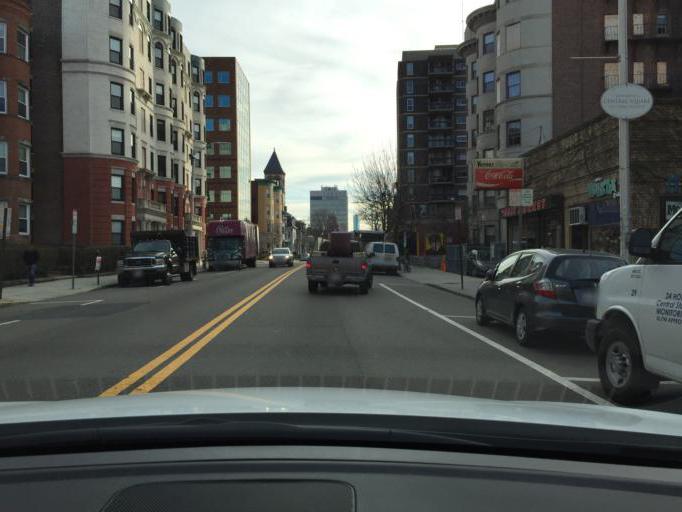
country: US
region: Massachusetts
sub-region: Middlesex County
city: Cambridge
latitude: 42.3682
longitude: -71.1084
